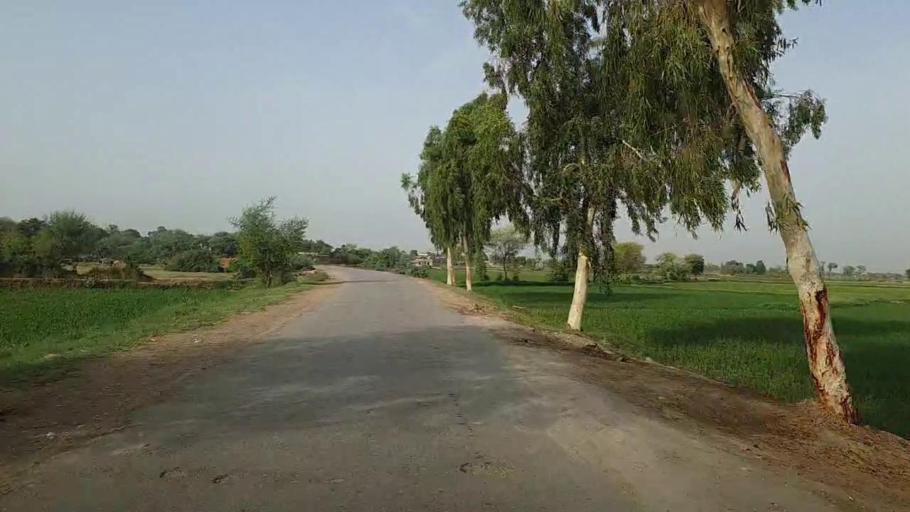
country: PK
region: Sindh
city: Khairpur Nathan Shah
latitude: 27.1198
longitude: 67.7885
